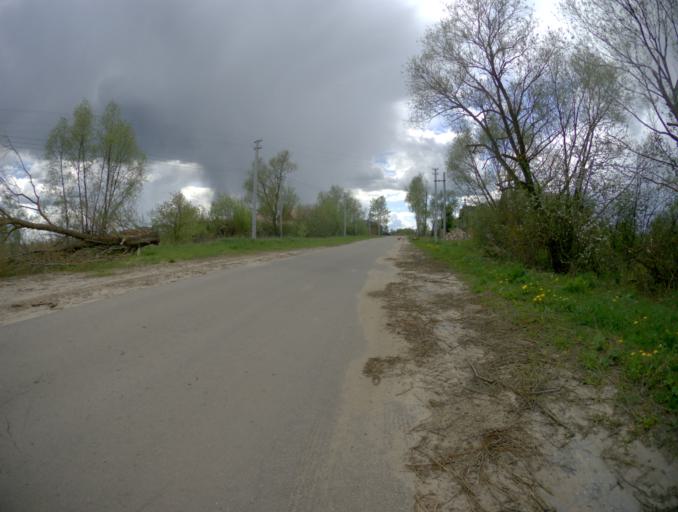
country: RU
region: Vladimir
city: Velikodvorskiy
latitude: 55.2660
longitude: 40.7960
